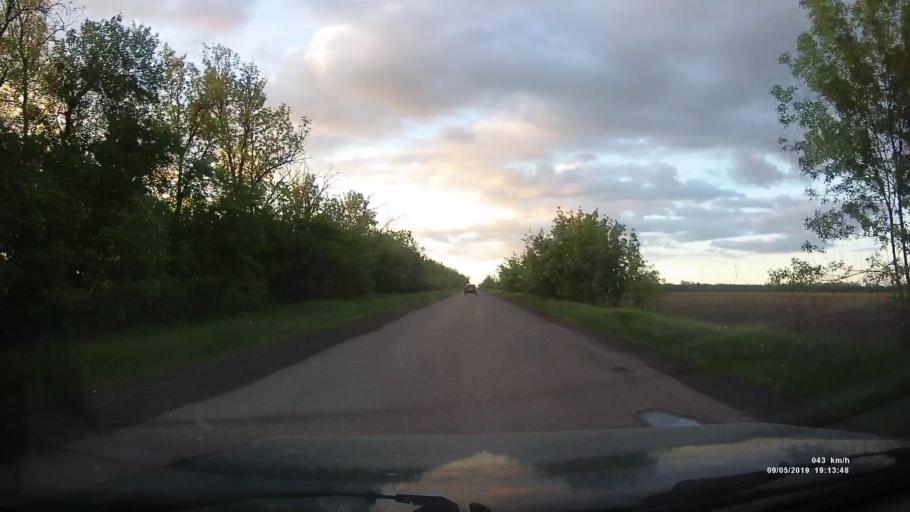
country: RU
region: Krasnodarskiy
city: Kanelovskaya
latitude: 46.7530
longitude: 39.2139
